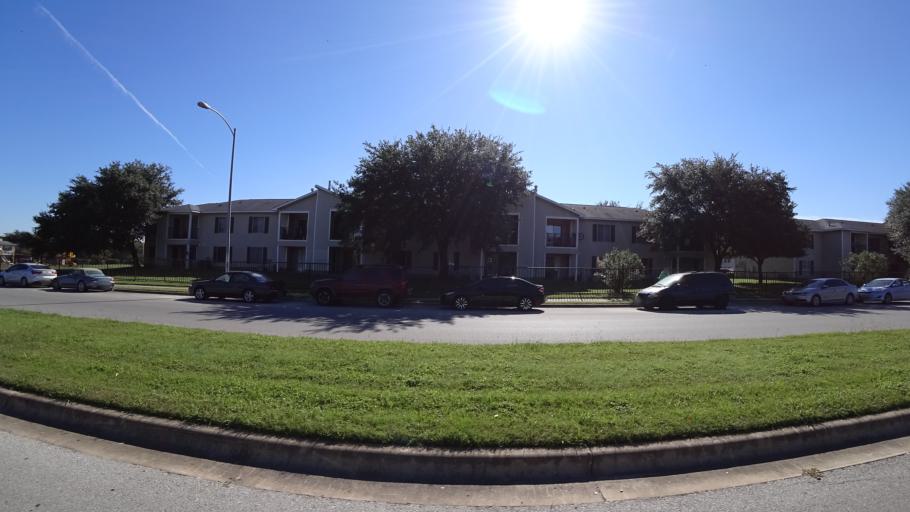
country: US
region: Texas
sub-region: Travis County
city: Austin
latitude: 30.2346
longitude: -97.7152
